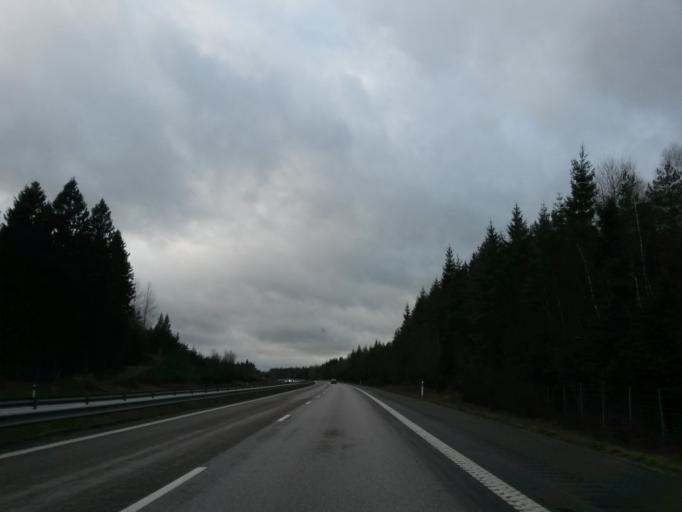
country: SE
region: Vaestra Goetaland
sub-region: Boras Kommun
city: Sandared
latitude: 57.6833
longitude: 12.7552
